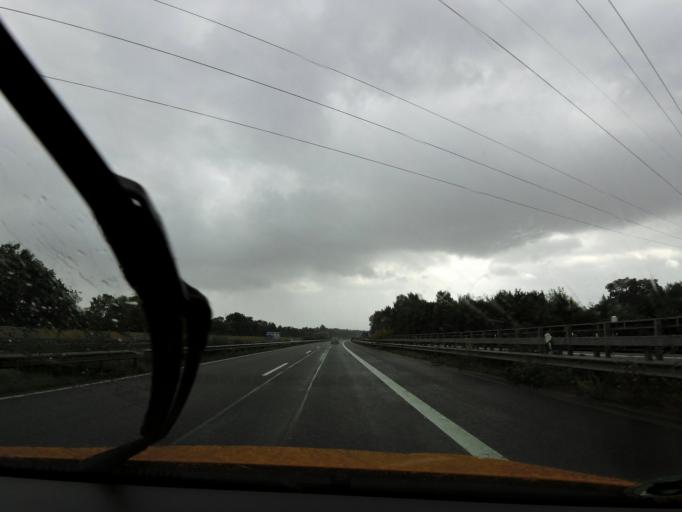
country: DE
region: Lower Saxony
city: Oldenburg
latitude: 53.1188
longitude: 8.2635
